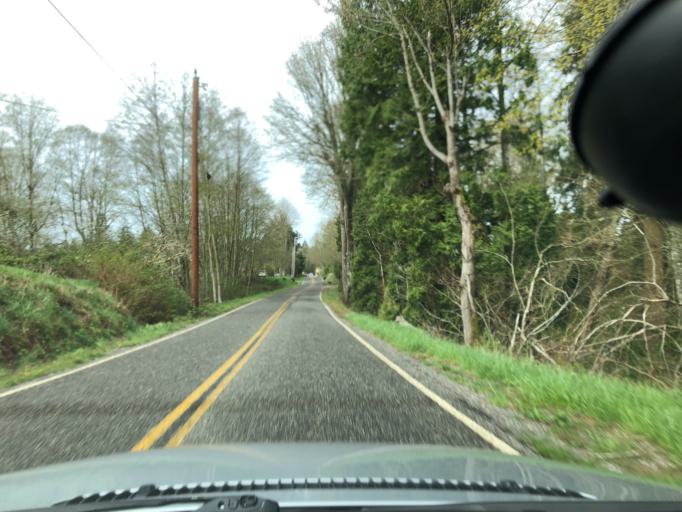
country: US
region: Washington
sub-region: Whatcom County
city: Blaine
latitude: 48.9717
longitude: -122.6990
